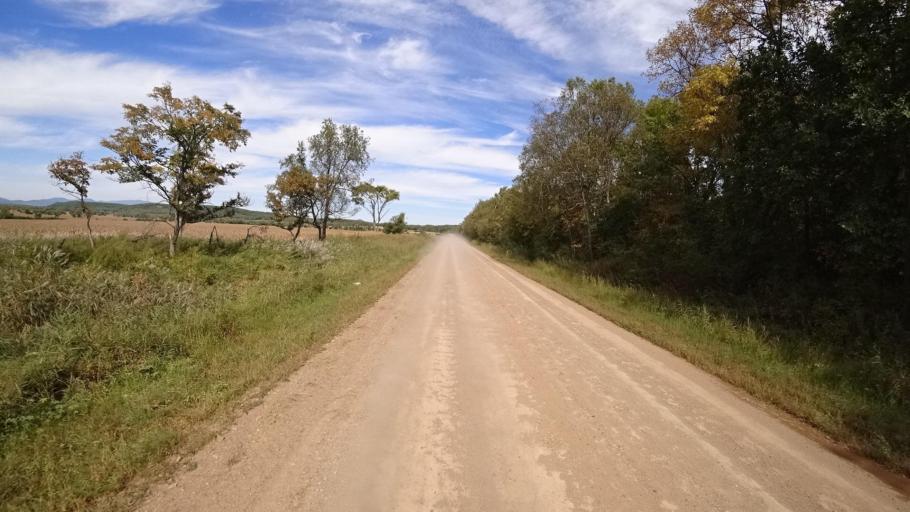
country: RU
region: Primorskiy
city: Yakovlevka
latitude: 44.5825
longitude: 133.5997
